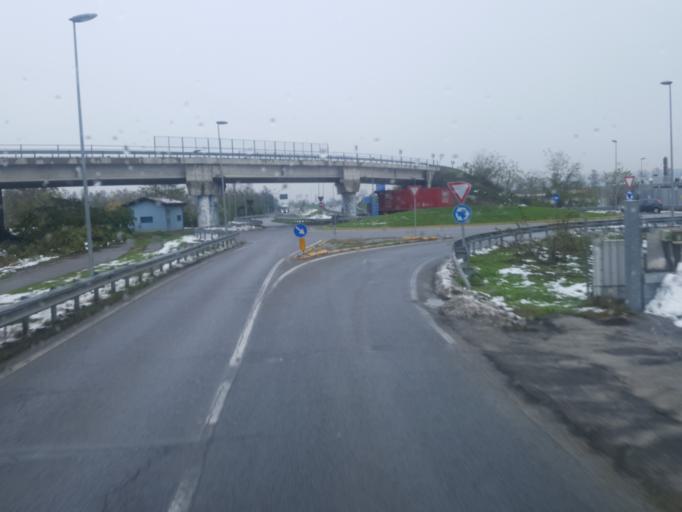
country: IT
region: Piedmont
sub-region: Provincia di Cuneo
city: Breo
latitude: 44.4189
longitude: 7.8466
